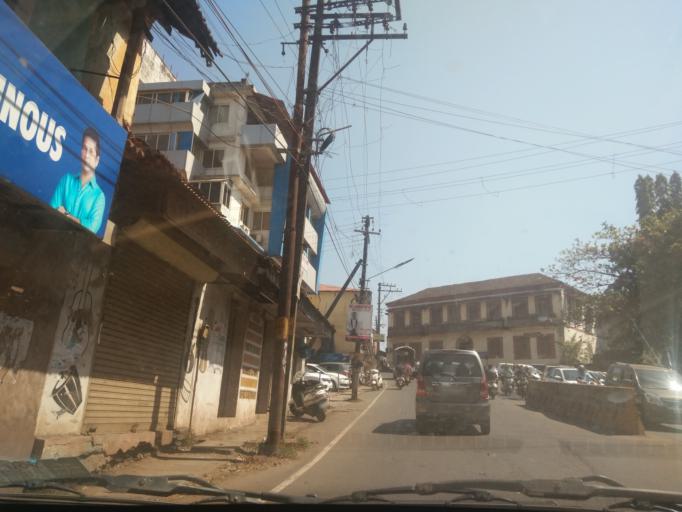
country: IN
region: Goa
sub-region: North Goa
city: Mapuca
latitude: 15.5908
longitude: 73.8121
